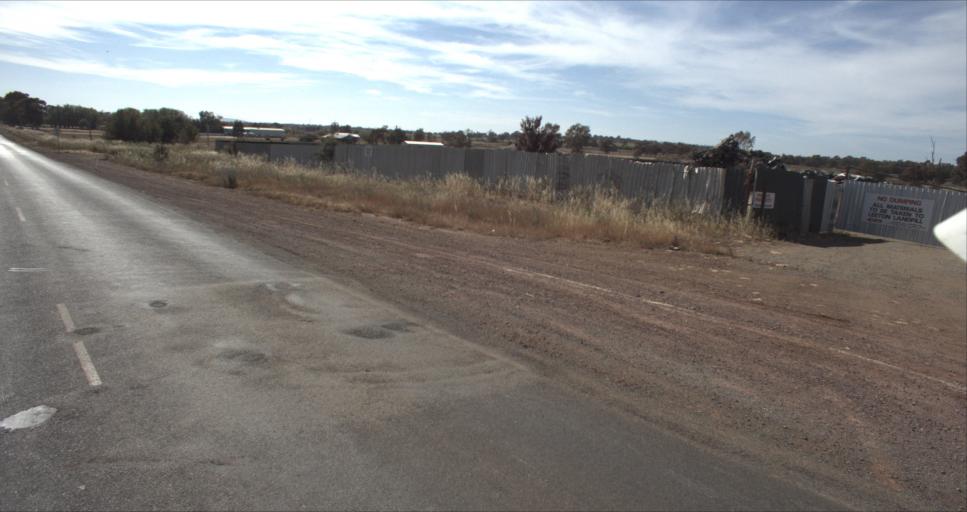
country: AU
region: New South Wales
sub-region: Leeton
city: Leeton
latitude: -34.5644
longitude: 146.4263
